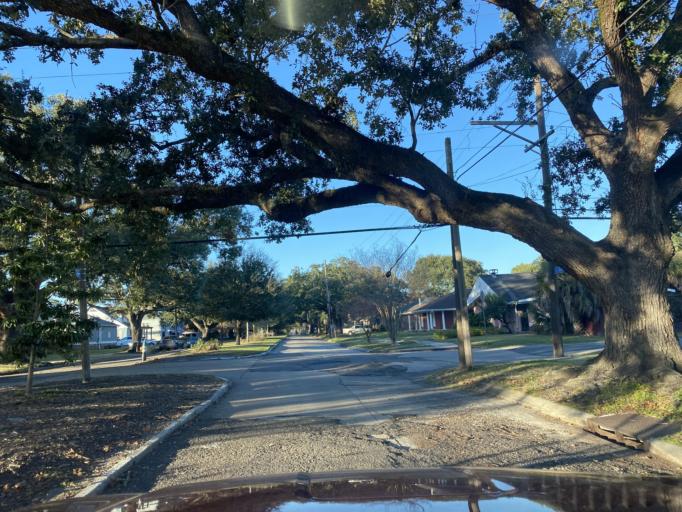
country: US
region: Louisiana
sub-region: Orleans Parish
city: New Orleans
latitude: 30.0100
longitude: -90.0555
